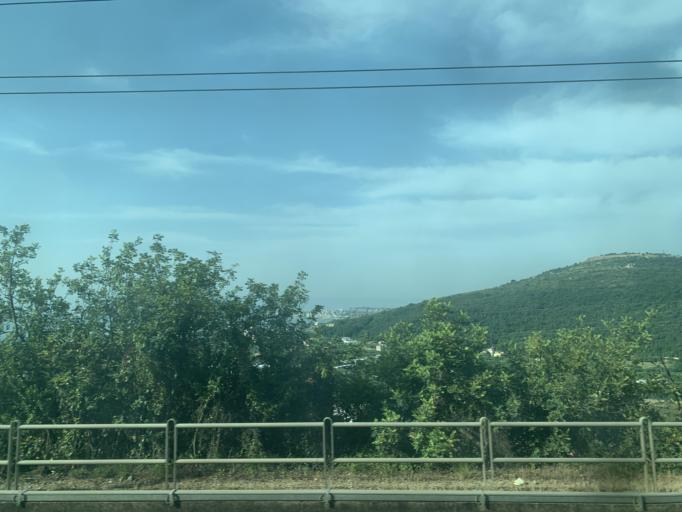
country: IT
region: Latium
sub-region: Provincia di Latina
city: Gaeta
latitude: 41.2538
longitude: 13.5789
